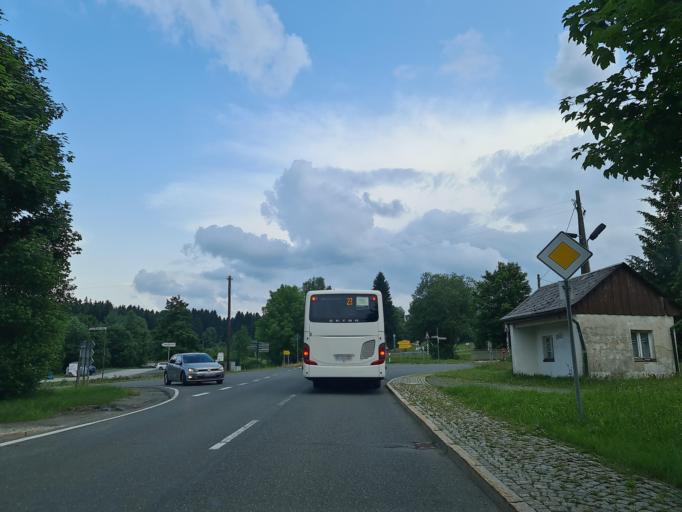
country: DE
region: Saxony
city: Hammerbrucke
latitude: 50.4170
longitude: 12.4012
